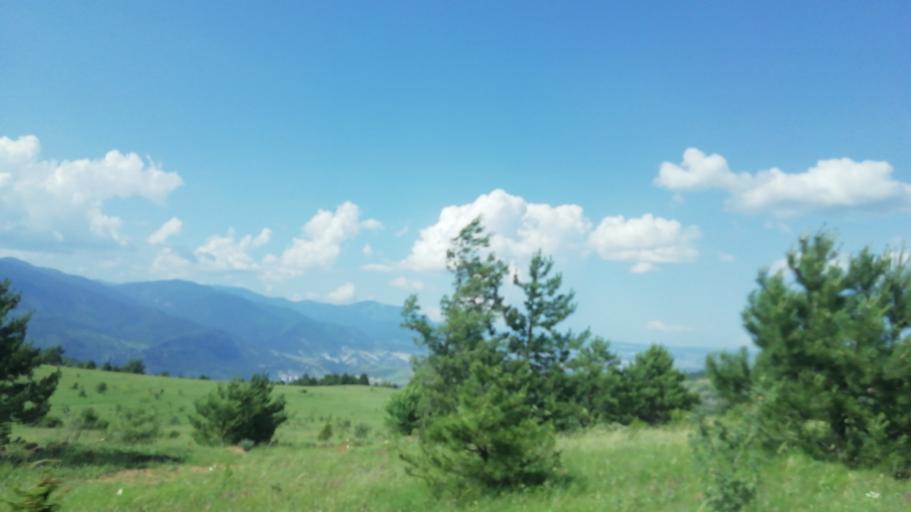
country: TR
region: Karabuk
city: Karabuk
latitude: 41.1306
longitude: 32.5759
